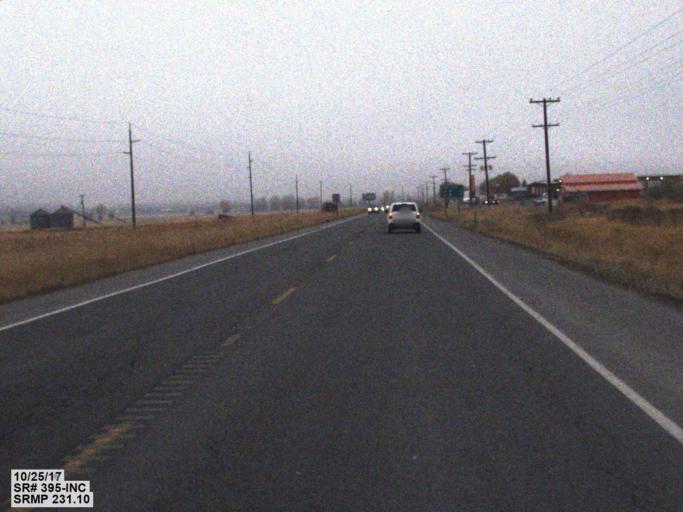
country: US
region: Washington
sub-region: Stevens County
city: Colville
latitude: 48.5599
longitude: -117.9281
